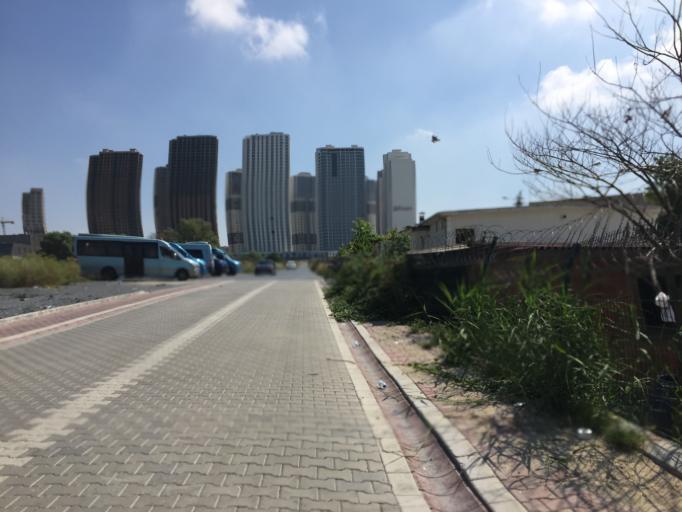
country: TR
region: Istanbul
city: Esenyurt
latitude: 41.0678
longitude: 28.6549
